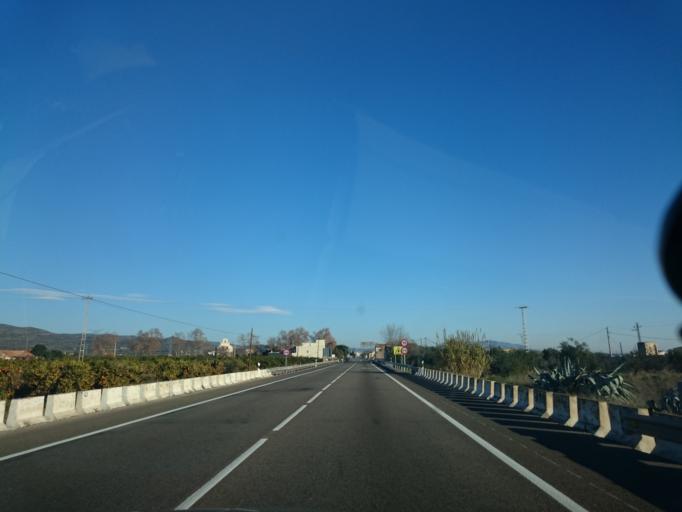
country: ES
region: Valencia
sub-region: Provincia de Castello
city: Orpesa/Oropesa del Mar
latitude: 40.1366
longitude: 0.1503
